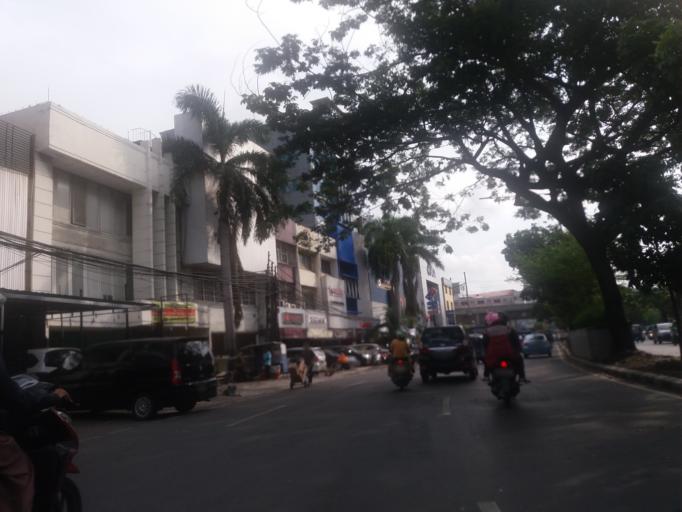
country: ID
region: Jakarta Raya
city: Jakarta
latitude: -6.1623
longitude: 106.8299
